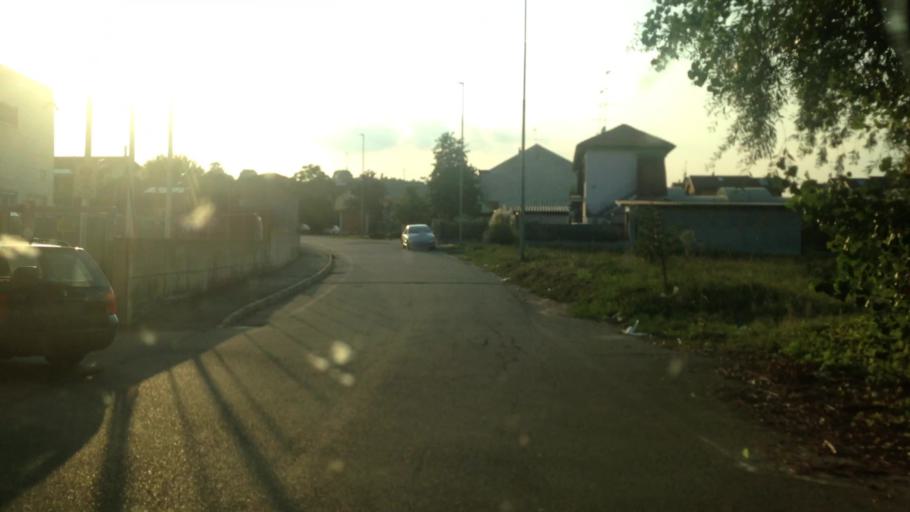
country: IT
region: Piedmont
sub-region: Provincia di Asti
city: Asti
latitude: 44.9163
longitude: 8.2277
